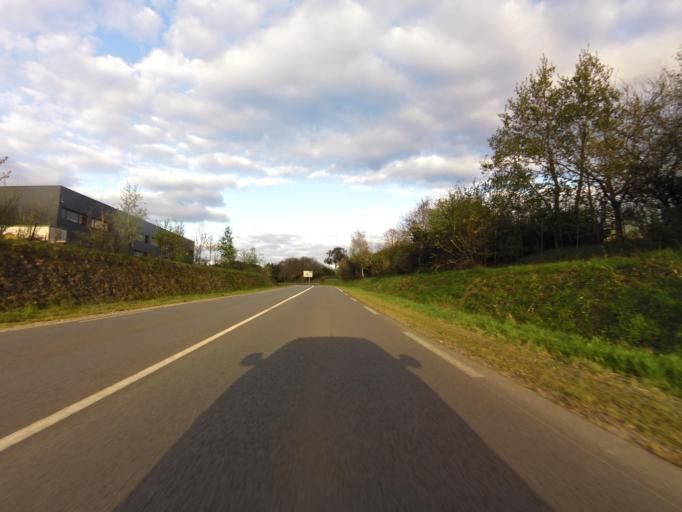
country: FR
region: Brittany
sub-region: Departement du Morbihan
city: Plougoumelen
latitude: 47.6616
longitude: -2.9082
